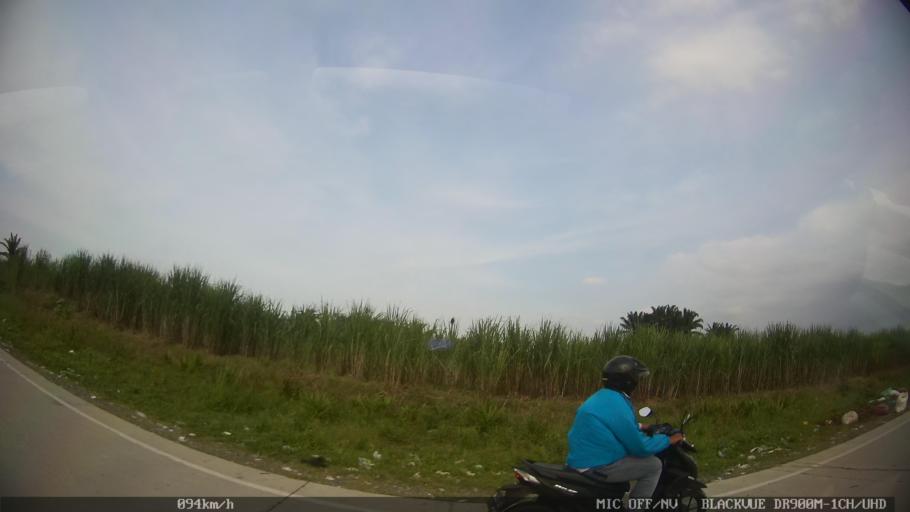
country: ID
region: North Sumatra
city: Binjai
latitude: 3.5966
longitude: 98.5329
